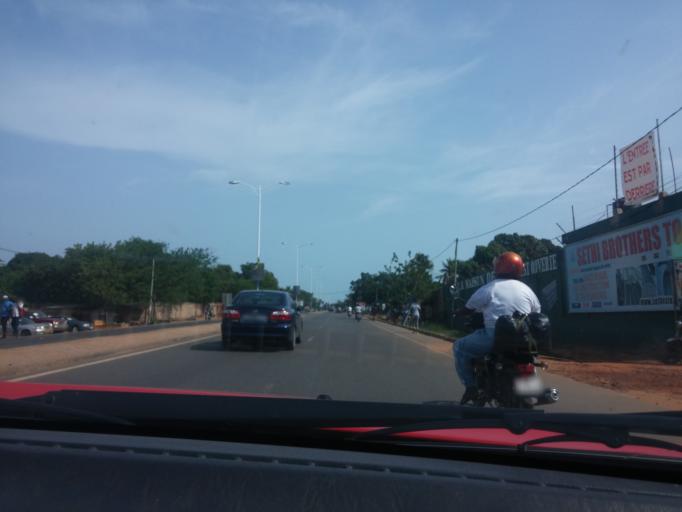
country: TG
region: Maritime
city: Lome
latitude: 6.2375
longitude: 1.2104
